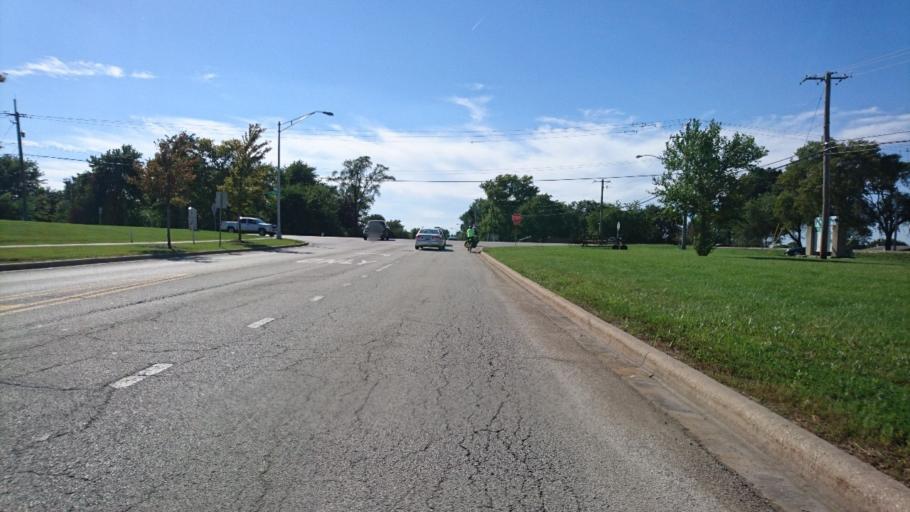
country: US
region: Illinois
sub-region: Will County
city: Ingalls Park
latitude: 41.5110
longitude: -88.0228
